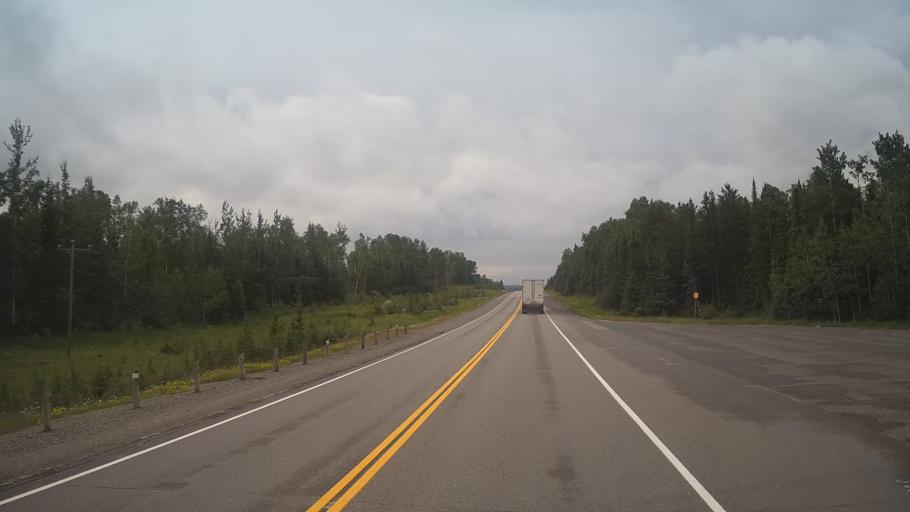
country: CA
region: Ontario
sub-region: Thunder Bay District
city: Thunder Bay
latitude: 48.7152
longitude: -89.8870
